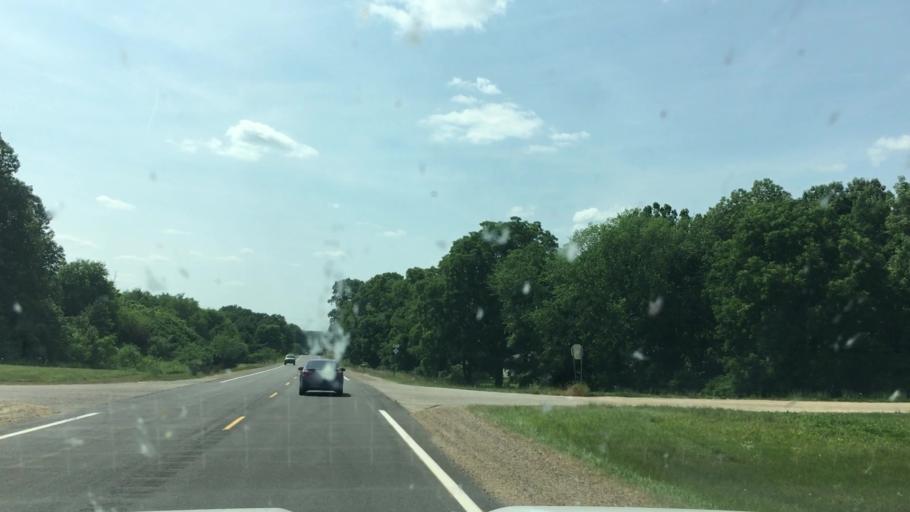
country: US
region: Michigan
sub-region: Allegan County
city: Plainwell
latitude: 42.4344
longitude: -85.5627
